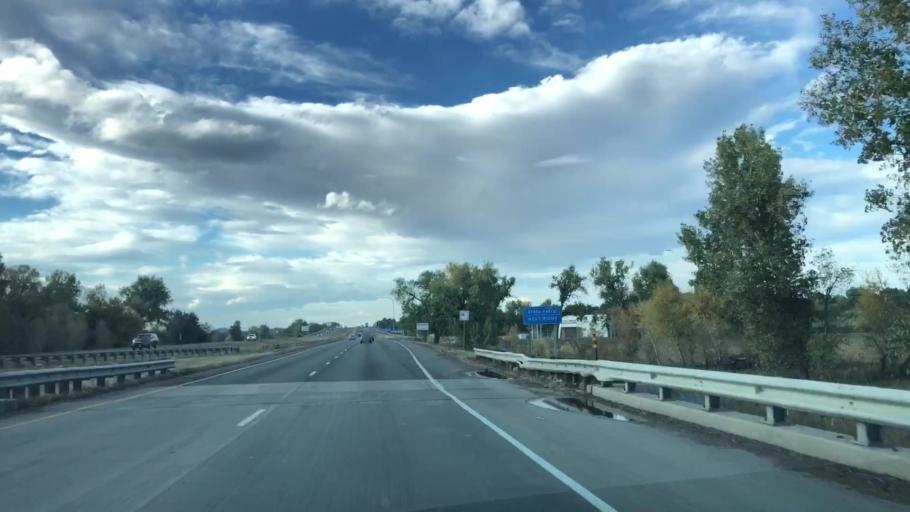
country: US
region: Colorado
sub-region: Larimer County
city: Fort Collins
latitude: 40.5315
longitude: -104.9933
